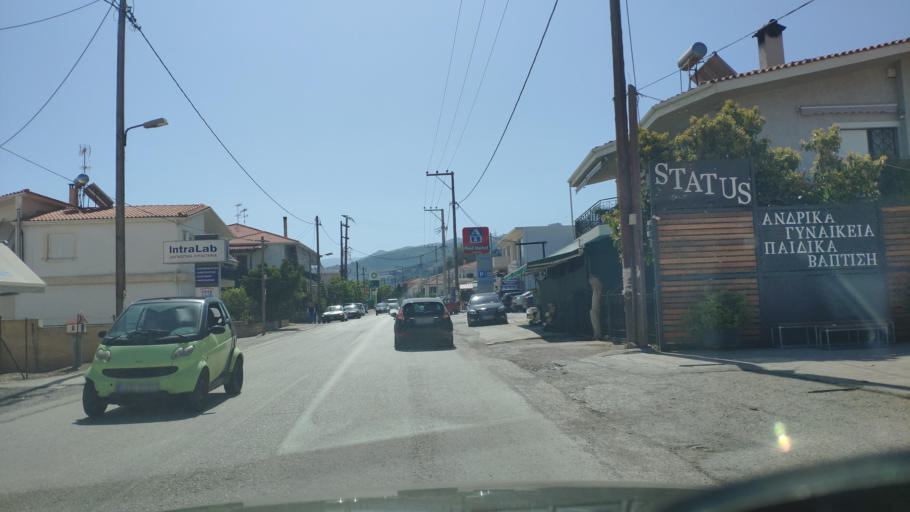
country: GR
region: West Greece
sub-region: Nomos Achaias
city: Aiyira
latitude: 38.1520
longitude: 22.3486
